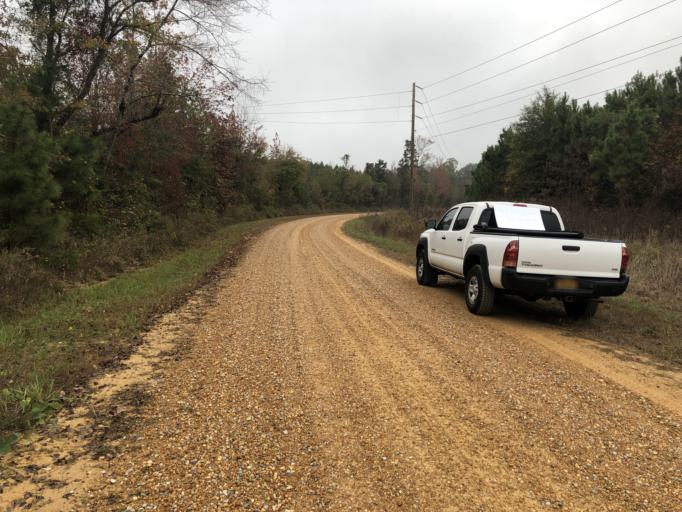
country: US
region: Mississippi
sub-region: Pontotoc County
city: Pontotoc
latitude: 34.3620
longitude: -89.2190
